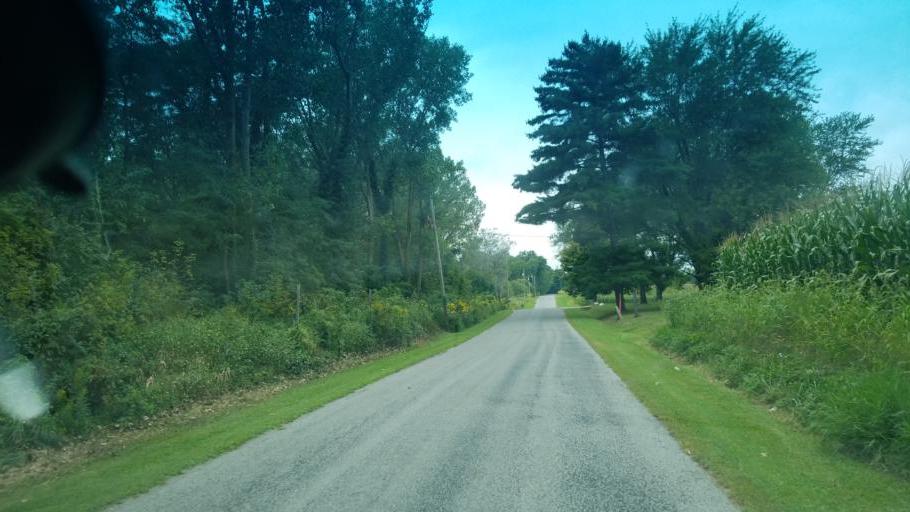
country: US
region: Ohio
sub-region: Richland County
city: Shelby
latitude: 40.9158
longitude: -82.6433
